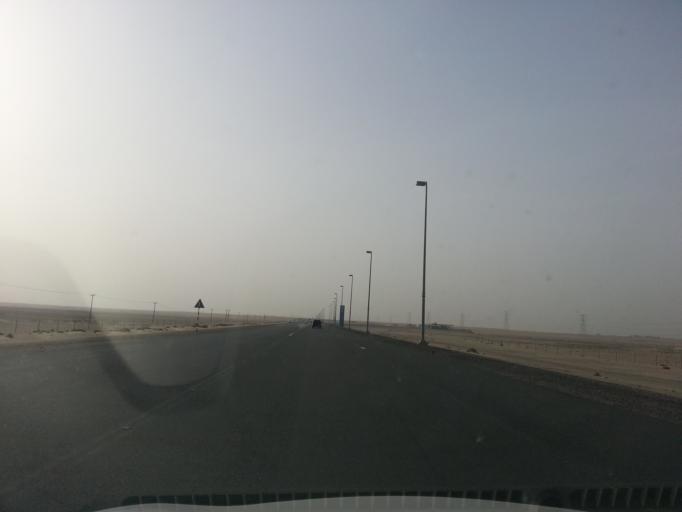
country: AE
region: Dubai
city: Dubai
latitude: 24.7979
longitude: 55.0732
